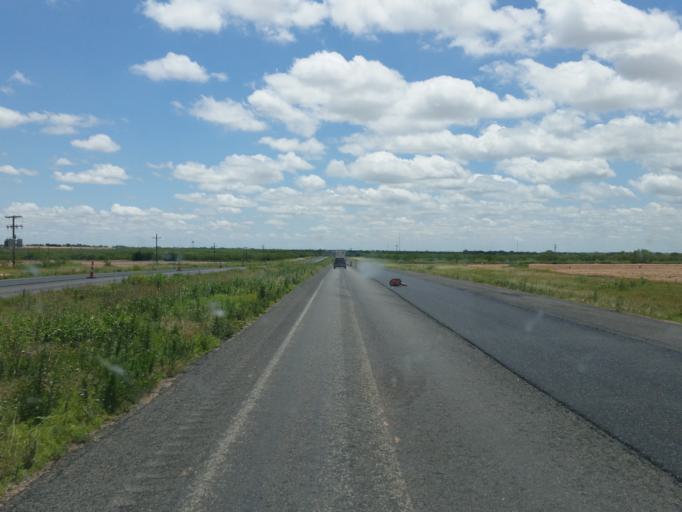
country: US
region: Texas
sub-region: Scurry County
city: Snyder
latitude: 32.7742
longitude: -100.9407
